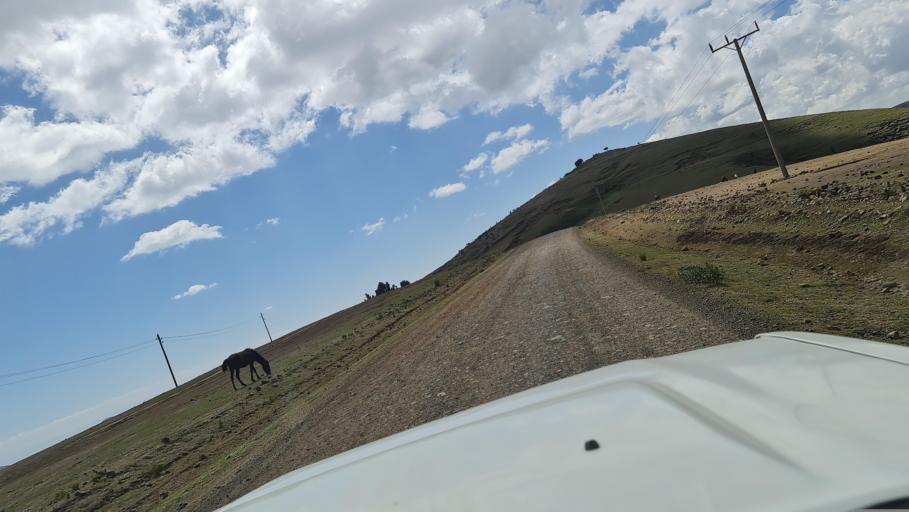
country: ET
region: Amhara
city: Debark'
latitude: 13.1953
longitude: 37.9742
